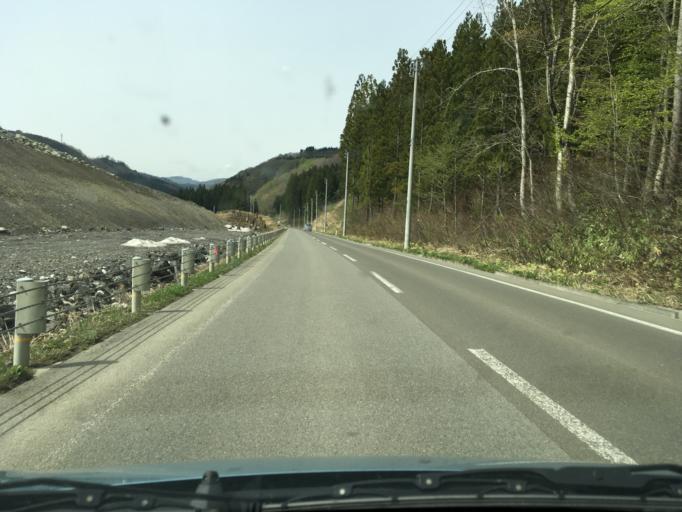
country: JP
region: Akita
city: Yuzawa
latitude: 39.0555
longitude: 140.7239
